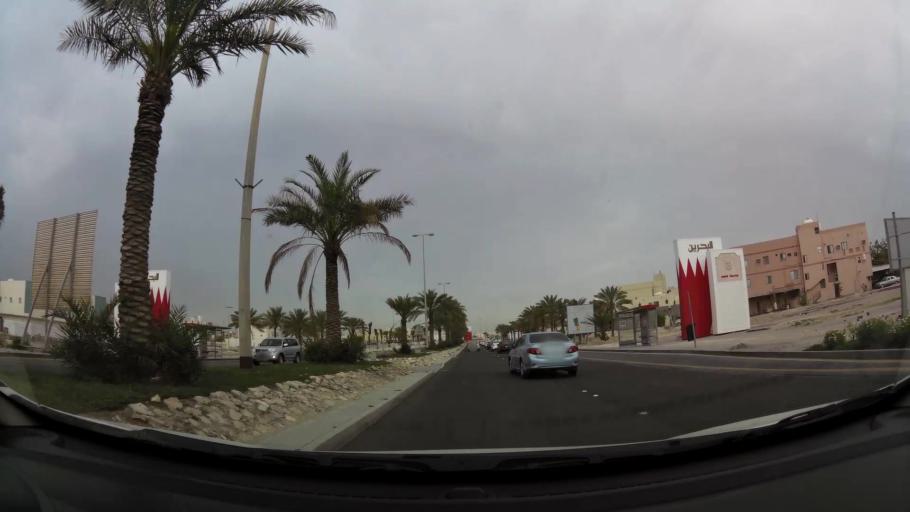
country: BH
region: Central Governorate
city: Dar Kulayb
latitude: 26.0604
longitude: 50.5084
